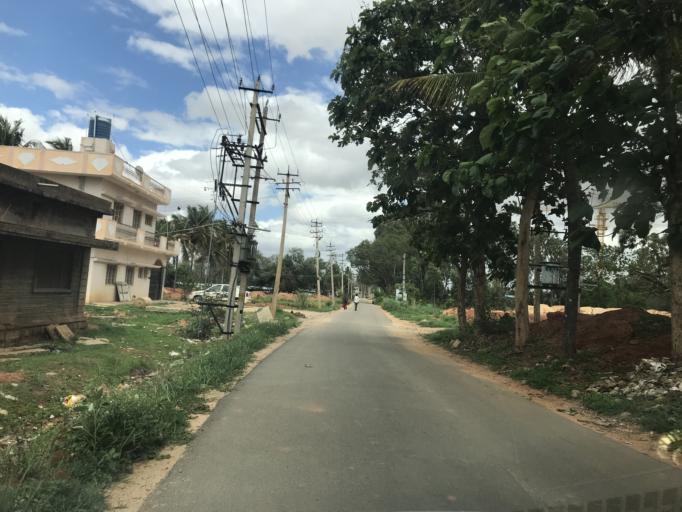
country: IN
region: Karnataka
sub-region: Bangalore Rural
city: Devanhalli
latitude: 13.2160
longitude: 77.6580
